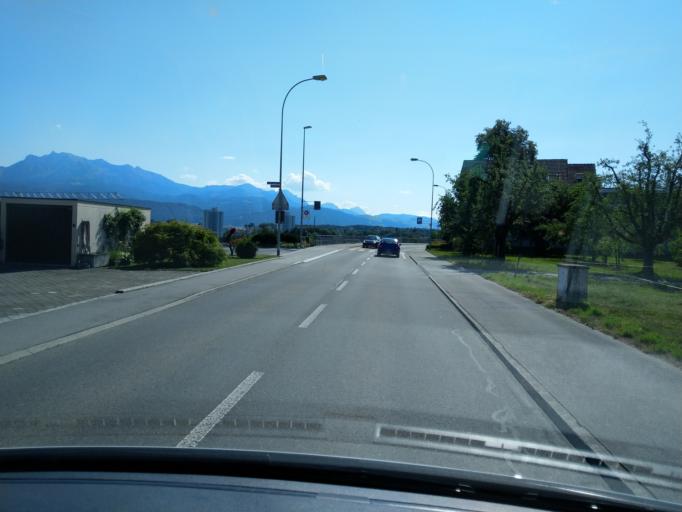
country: CH
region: Lucerne
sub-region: Hochdorf District
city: Emmen
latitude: 47.1002
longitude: 8.2824
